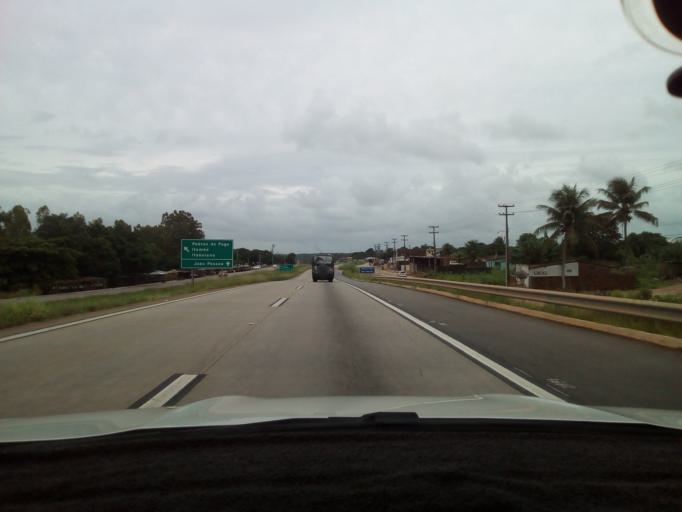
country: BR
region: Paraiba
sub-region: Alhandra
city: Alhandra
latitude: -7.3574
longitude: -34.9505
